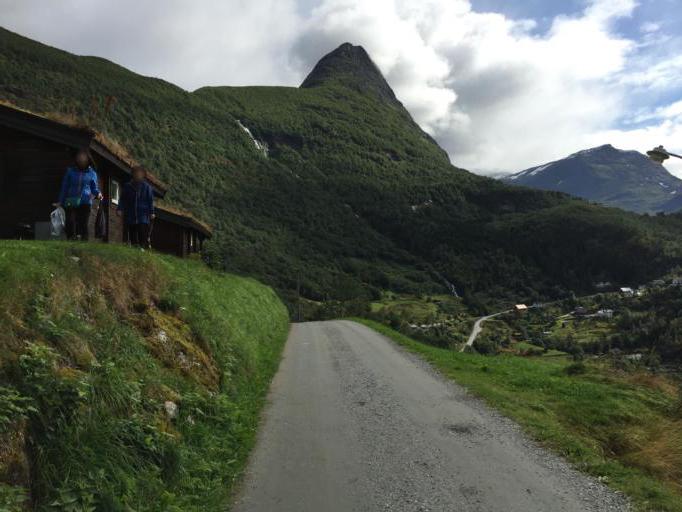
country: NO
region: More og Romsdal
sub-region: Norddal
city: Valldal
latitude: 62.1008
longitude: 7.2178
